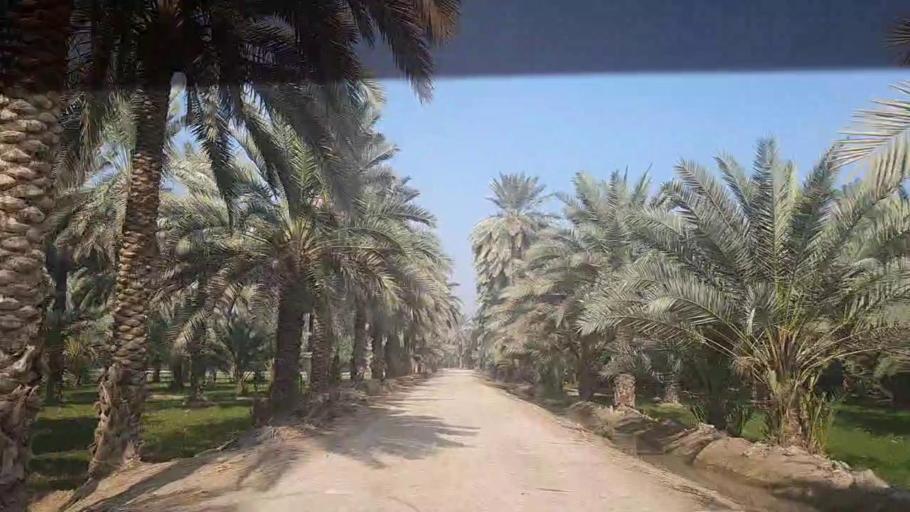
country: PK
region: Sindh
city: Khairpur
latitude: 27.4623
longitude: 68.7180
